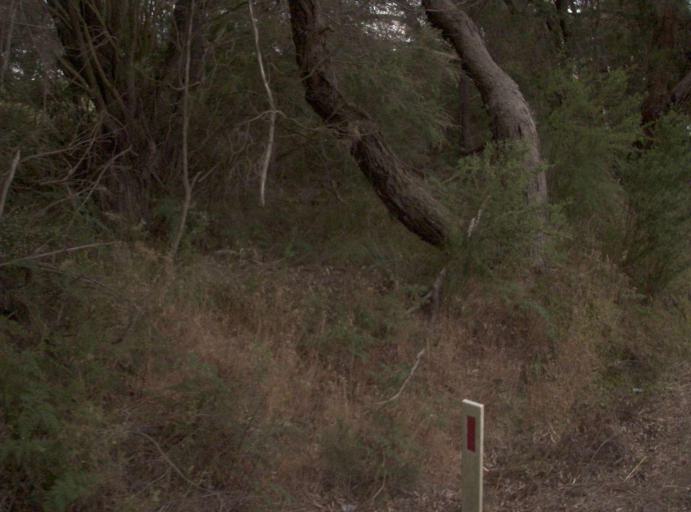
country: AU
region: Victoria
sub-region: East Gippsland
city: Bairnsdale
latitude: -37.9783
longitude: 147.4205
